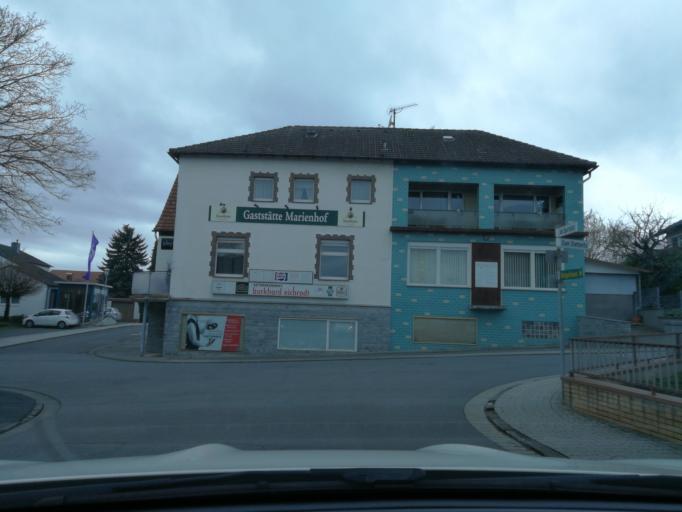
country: DE
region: Hesse
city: Reinheim
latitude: 49.8458
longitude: 8.8050
